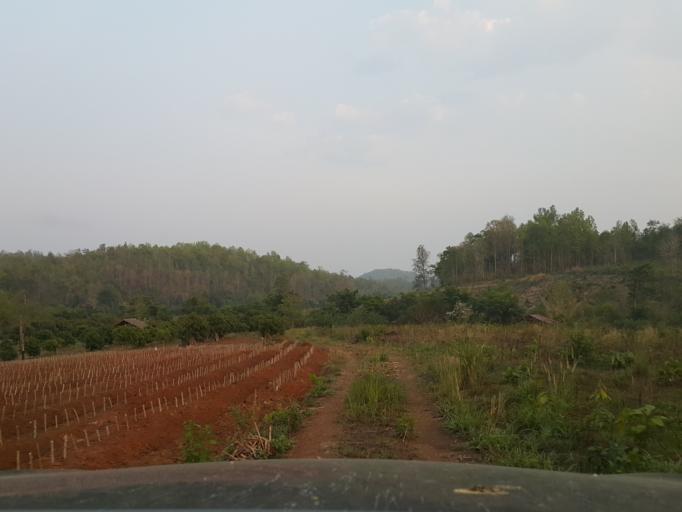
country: TH
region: Lamphun
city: Thung Hua Chang
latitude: 17.9104
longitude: 99.0753
